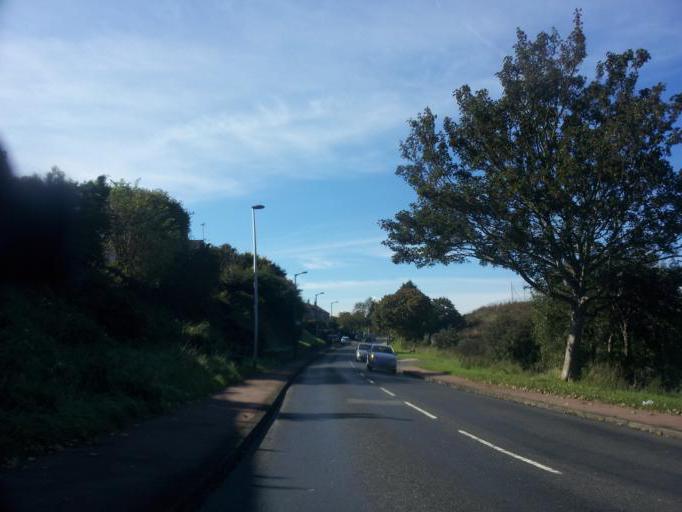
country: GB
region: England
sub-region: Kent
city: Chatham
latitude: 51.3664
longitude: 0.5401
